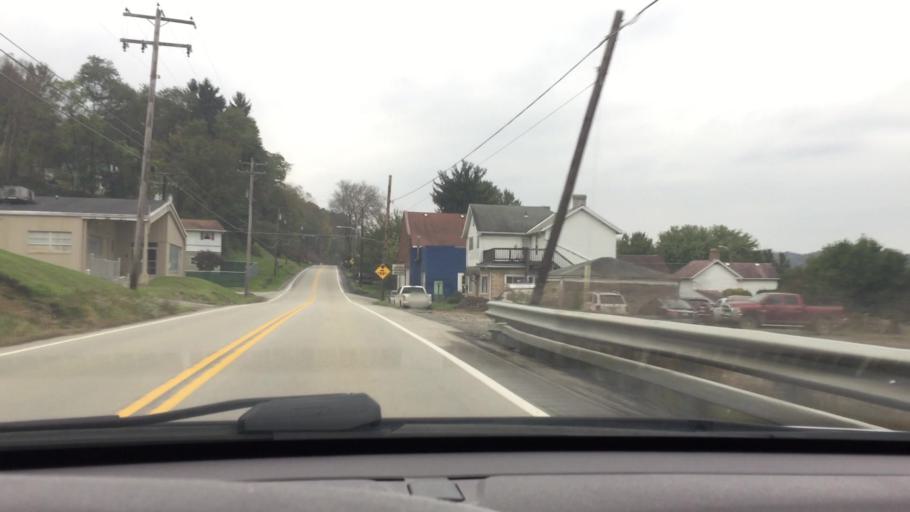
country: US
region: Pennsylvania
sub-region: Fayette County
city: Belle Vernon
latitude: 40.1156
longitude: -79.8623
